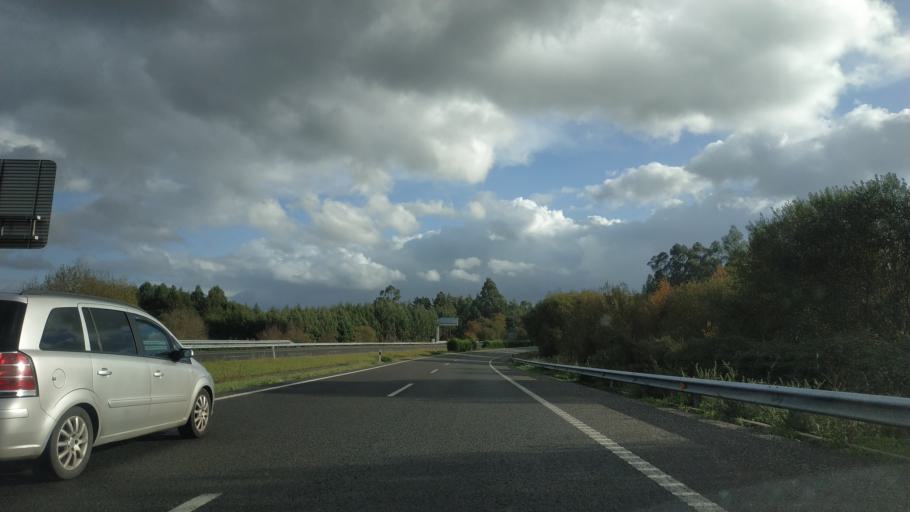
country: ES
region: Galicia
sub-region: Provincia da Coruna
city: Cambre
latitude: 43.2692
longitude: -8.3582
